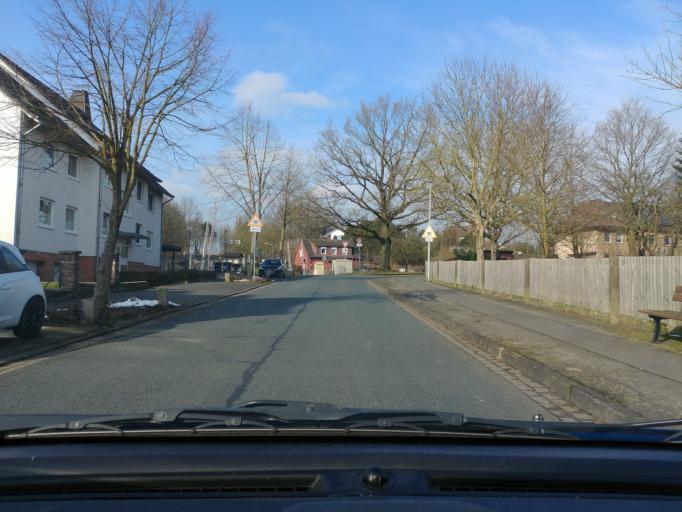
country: DE
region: Lower Saxony
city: Uslar
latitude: 51.6528
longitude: 9.6519
